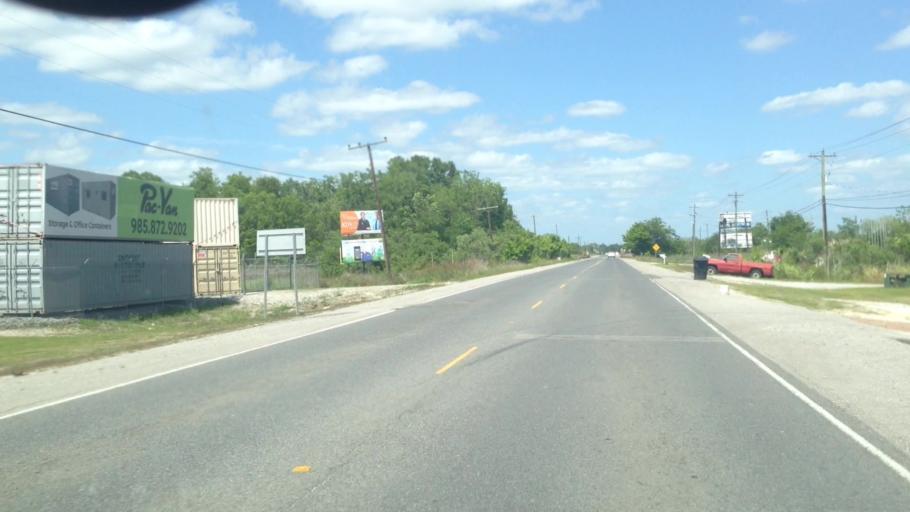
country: US
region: Louisiana
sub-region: Terrebonne Parish
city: Houma
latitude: 29.6512
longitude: -90.6826
